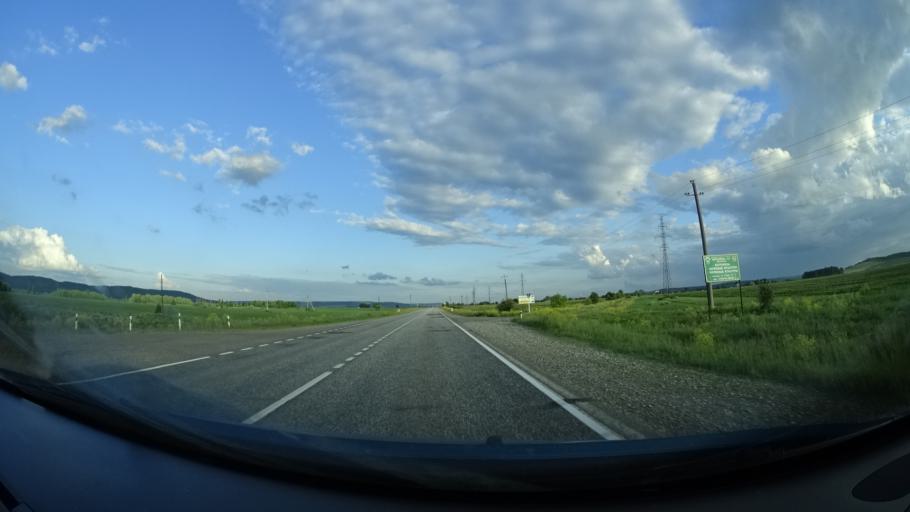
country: RU
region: Perm
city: Barda
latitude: 57.1020
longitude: 55.5282
